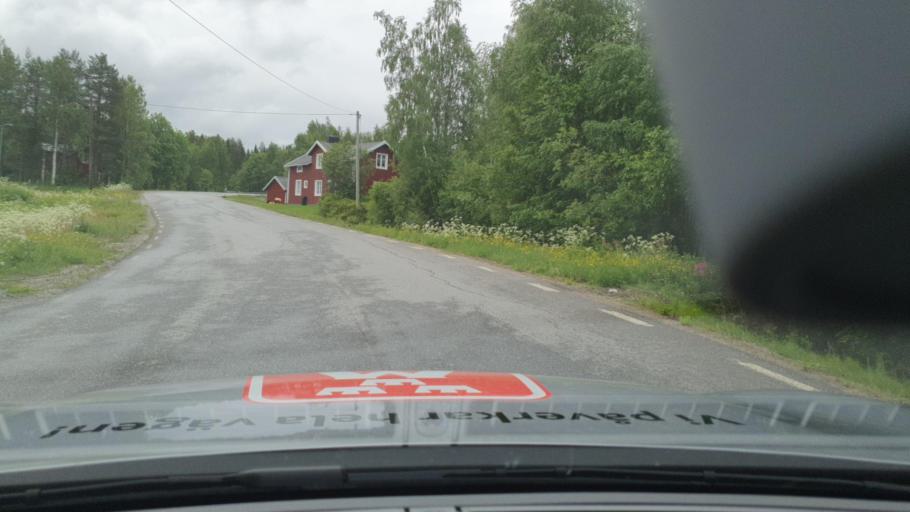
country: SE
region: Norrbotten
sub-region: Lulea Kommun
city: Ranea
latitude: 65.8462
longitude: 22.2912
